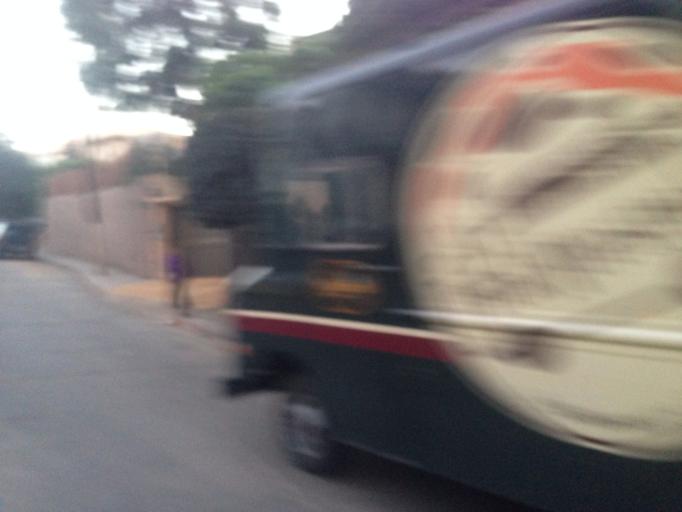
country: MX
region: Baja California
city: Tijuana
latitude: 32.5092
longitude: -117.0118
